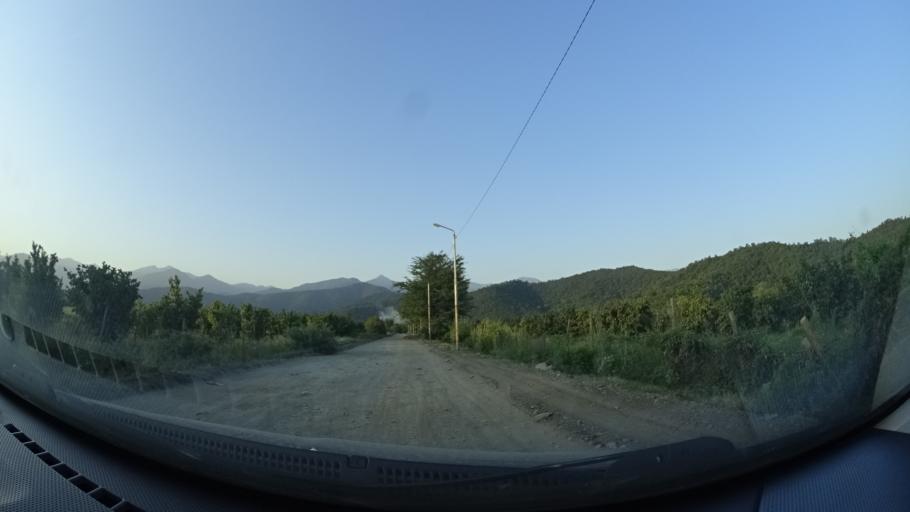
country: GE
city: Bagdadi
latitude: 41.8649
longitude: 46.0172
